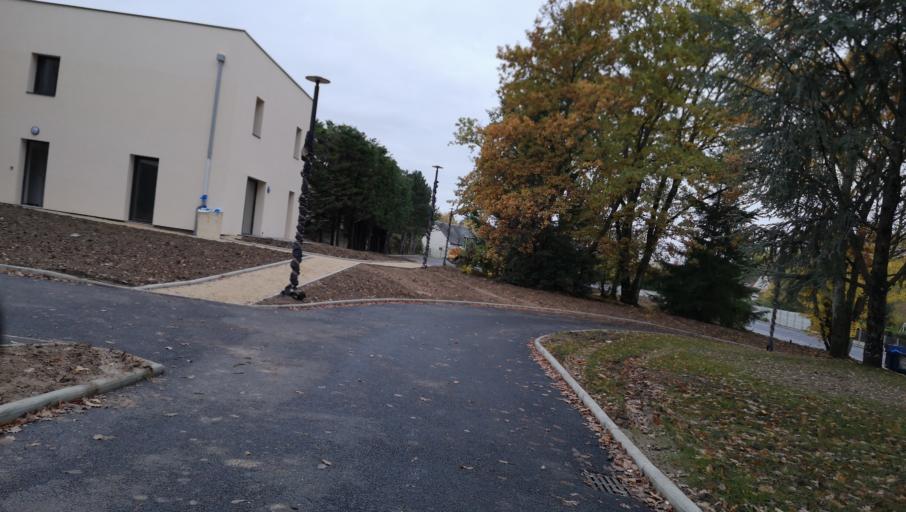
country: FR
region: Centre
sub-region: Departement du Loiret
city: Saint-Jean-de-Braye
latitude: 47.9056
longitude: 1.9674
